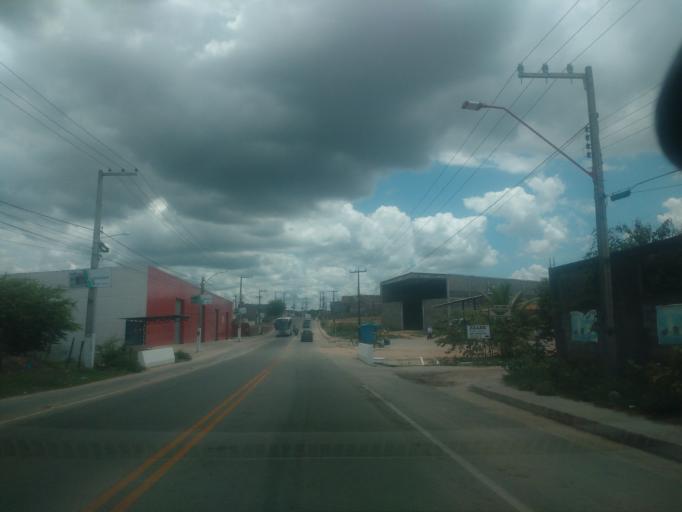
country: BR
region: Alagoas
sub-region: Uniao Dos Palmares
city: Uniao dos Palmares
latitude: -9.1531
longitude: -36.0183
